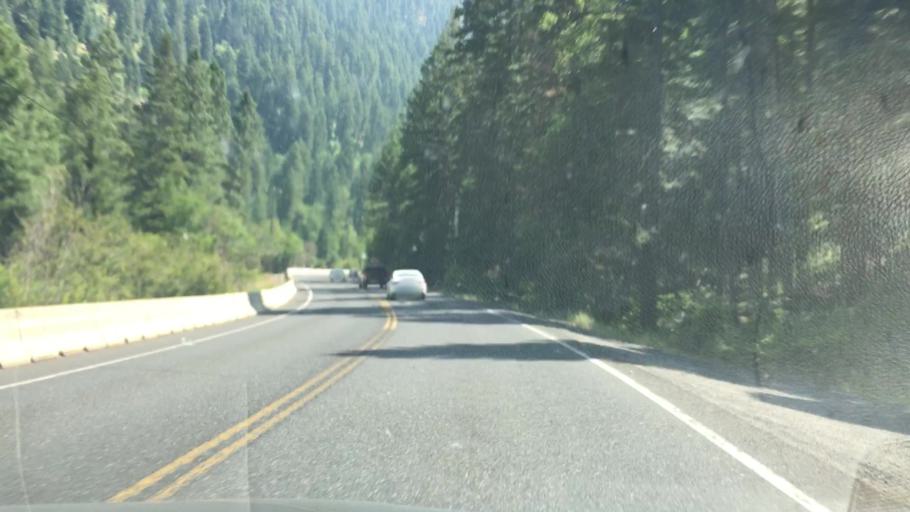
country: US
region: Idaho
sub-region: Valley County
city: McCall
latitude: 45.1386
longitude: -116.2858
